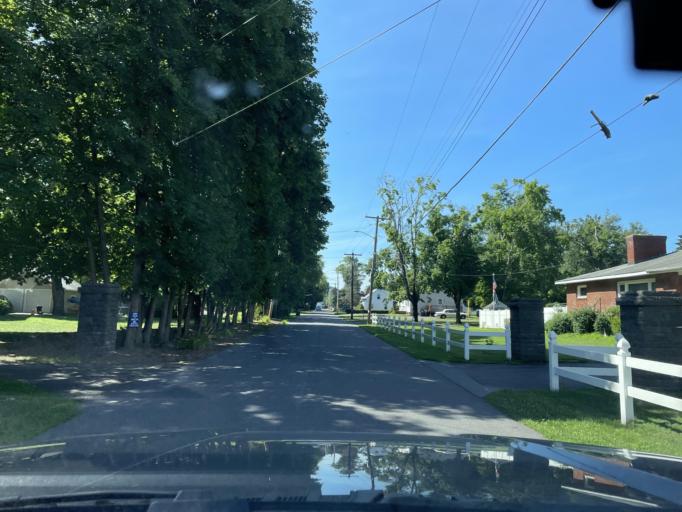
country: US
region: New York
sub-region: Ulster County
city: Saugerties South
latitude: 42.0622
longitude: -73.9537
